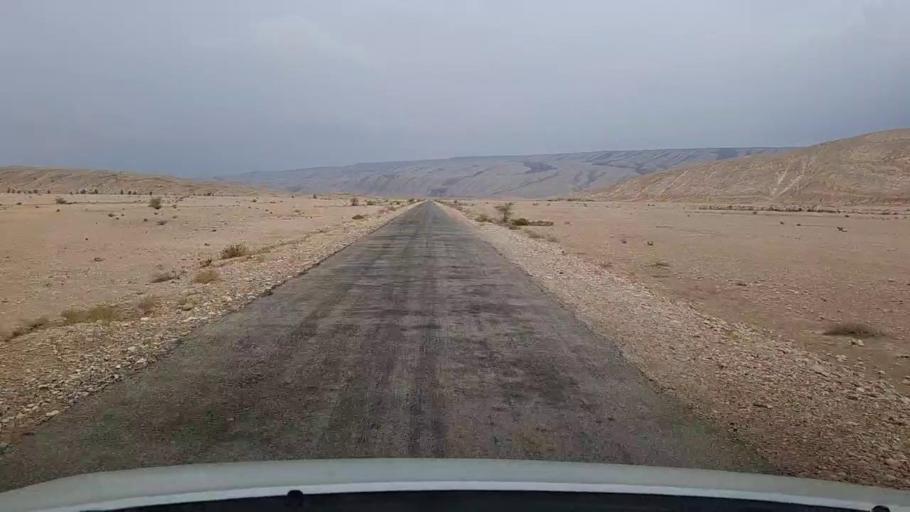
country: PK
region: Sindh
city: Sehwan
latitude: 26.2365
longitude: 67.7109
